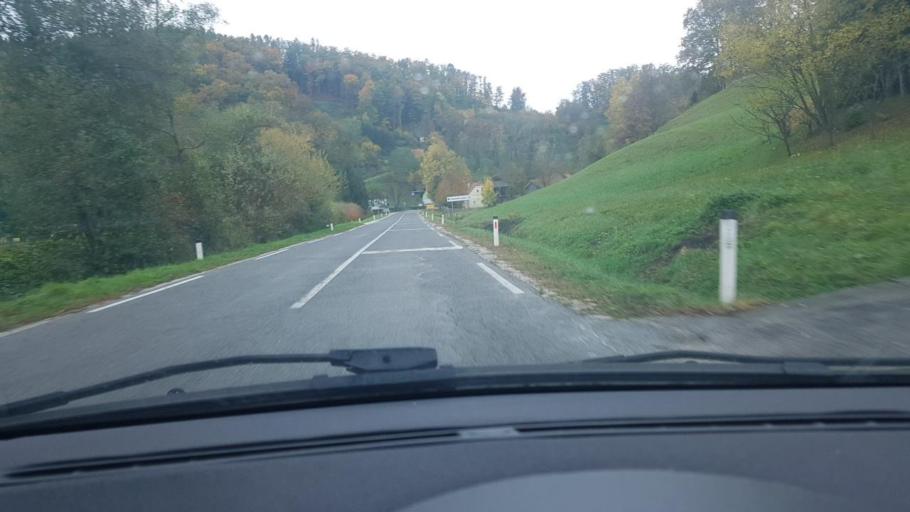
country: SI
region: Rogatec
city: Rogatec
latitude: 46.2362
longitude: 15.7027
